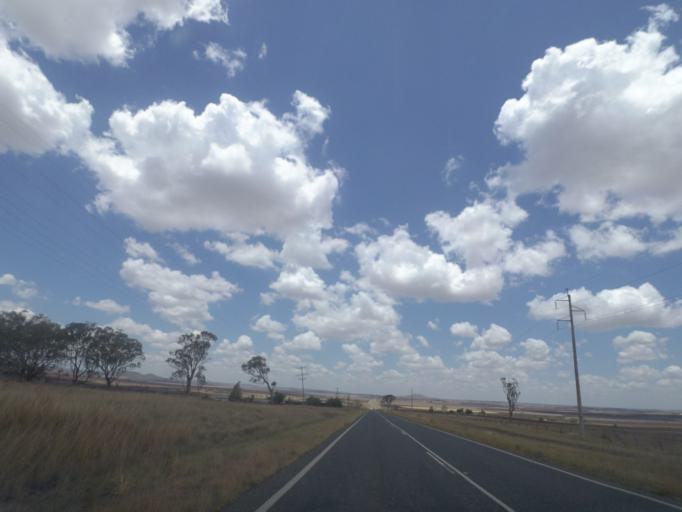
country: AU
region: Queensland
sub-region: Toowoomba
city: Top Camp
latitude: -27.8857
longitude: 151.9714
